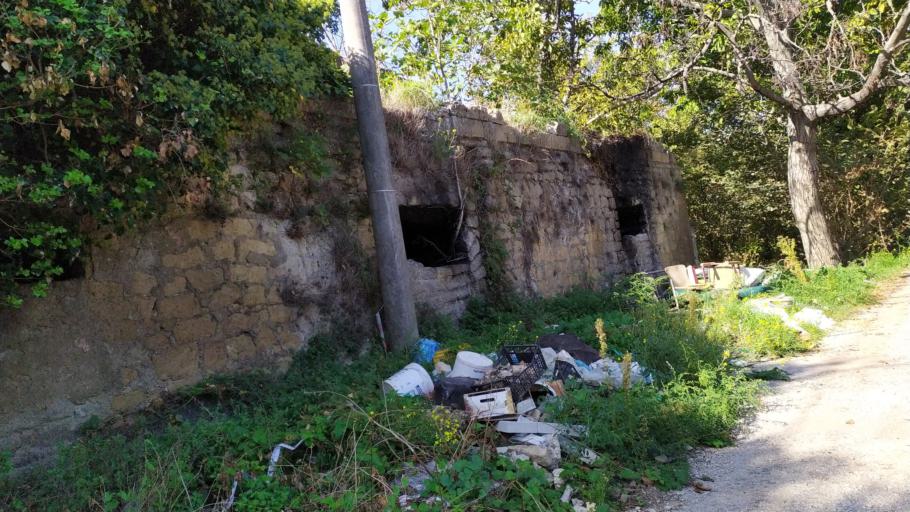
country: IT
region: Campania
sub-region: Provincia di Napoli
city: Camposano
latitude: 40.9635
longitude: 14.5176
